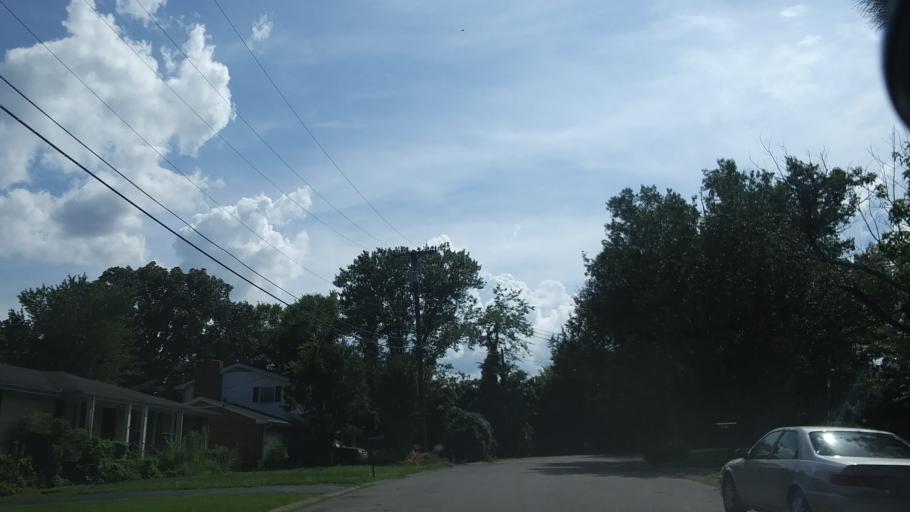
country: US
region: Tennessee
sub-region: Rutherford County
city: La Vergne
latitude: 36.0796
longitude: -86.6375
